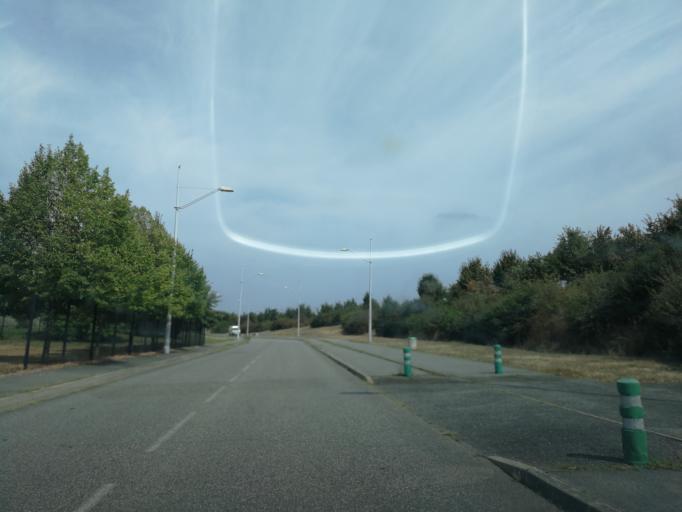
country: FR
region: Midi-Pyrenees
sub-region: Departement de la Haute-Garonne
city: Beauzelle
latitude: 43.6468
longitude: 1.3646
